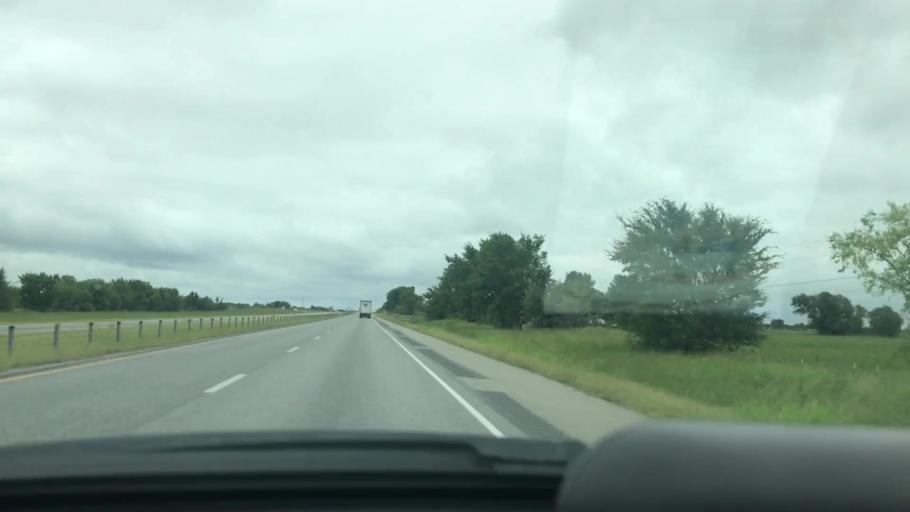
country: US
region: Oklahoma
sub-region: Pittsburg County
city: McAlester
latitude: 34.7469
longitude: -95.8956
